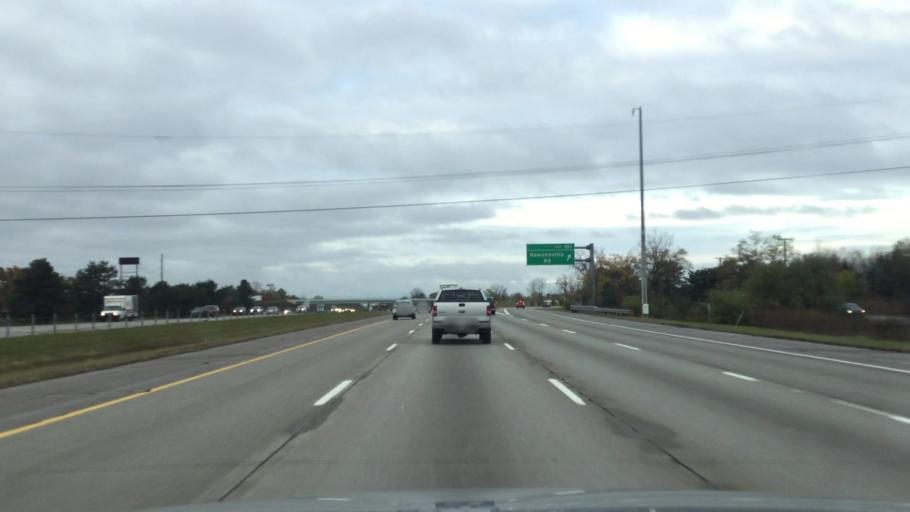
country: US
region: Michigan
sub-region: Wayne County
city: Belleville
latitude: 42.2189
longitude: -83.5386
